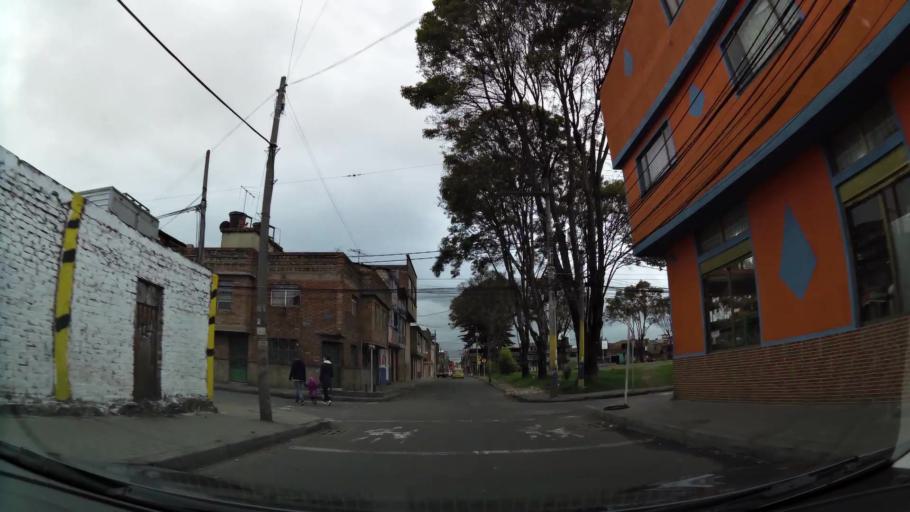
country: CO
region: Bogota D.C.
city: Bogota
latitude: 4.6824
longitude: -74.1019
